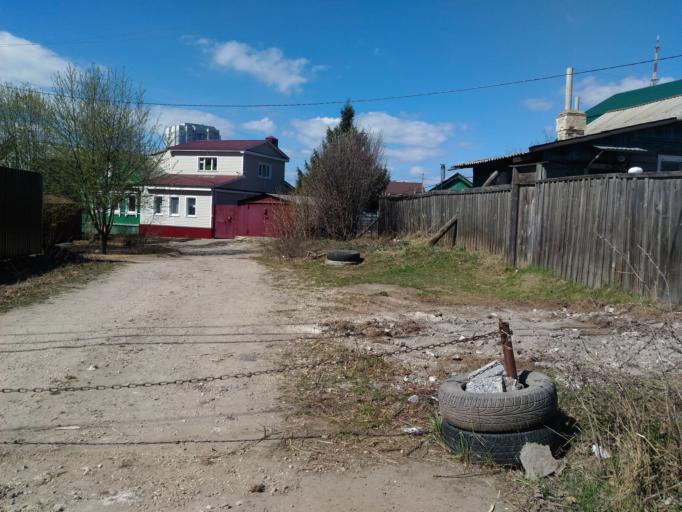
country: RU
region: Ulyanovsk
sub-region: Ulyanovskiy Rayon
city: Ulyanovsk
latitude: 54.3377
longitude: 48.3891
